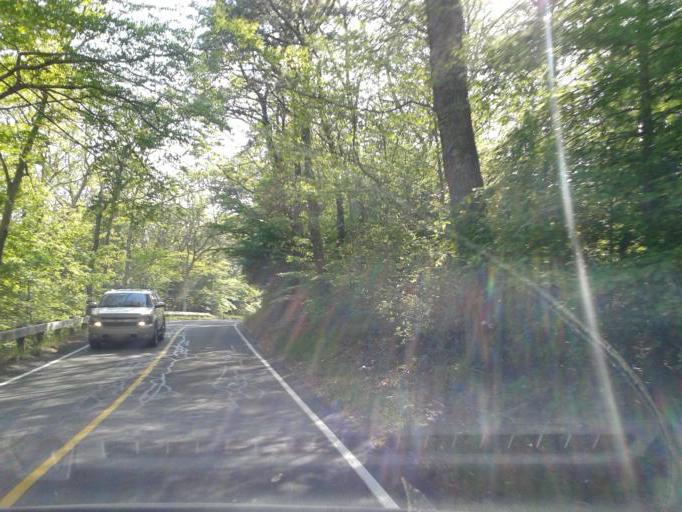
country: US
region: Massachusetts
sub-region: Barnstable County
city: Falmouth
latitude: 41.5291
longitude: -70.6502
